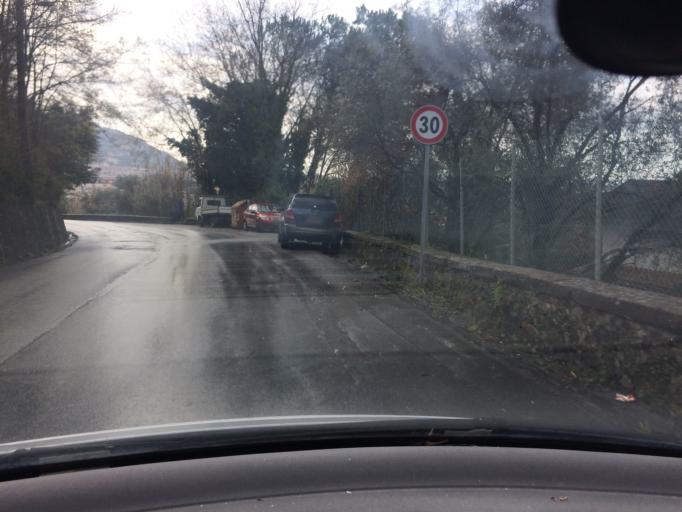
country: IT
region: Tuscany
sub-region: Provincia di Massa-Carrara
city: Massa
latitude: 44.0491
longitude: 10.1302
